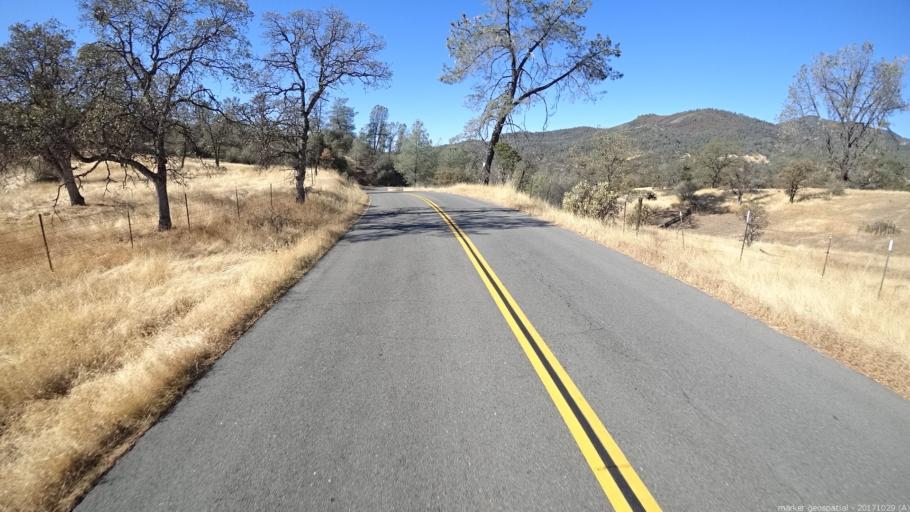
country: US
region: California
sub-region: Shasta County
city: Shasta
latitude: 40.4408
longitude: -122.7003
